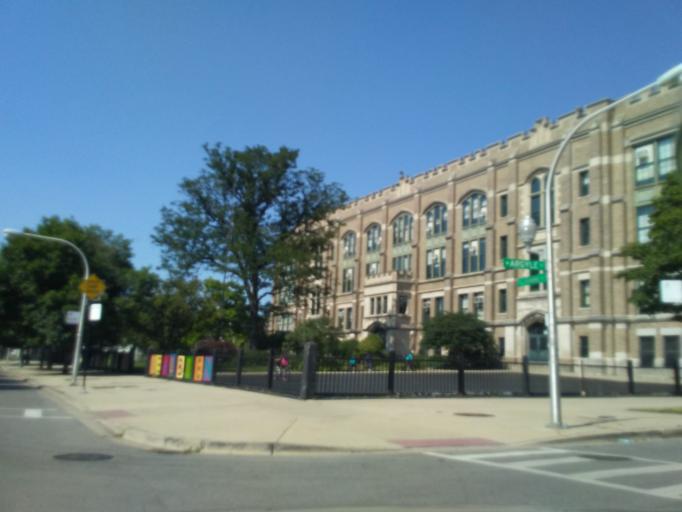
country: US
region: Illinois
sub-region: Cook County
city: Lincolnwood
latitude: 41.9715
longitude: -87.7575
